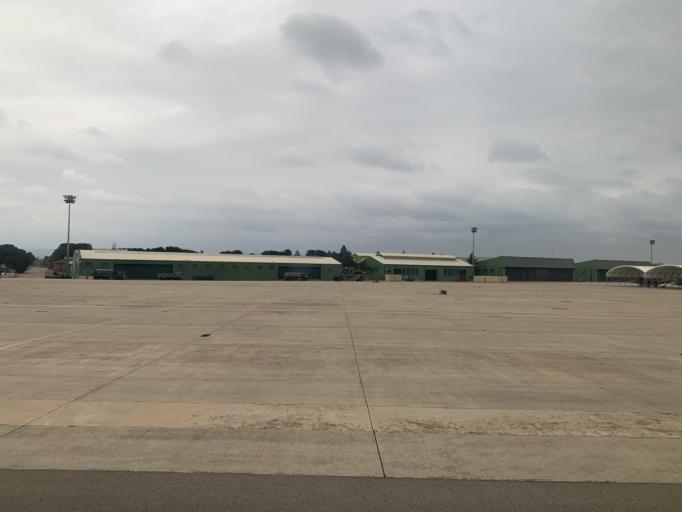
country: ES
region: Aragon
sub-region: Provincia de Zaragoza
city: Utebo
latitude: 41.6687
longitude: -1.0322
